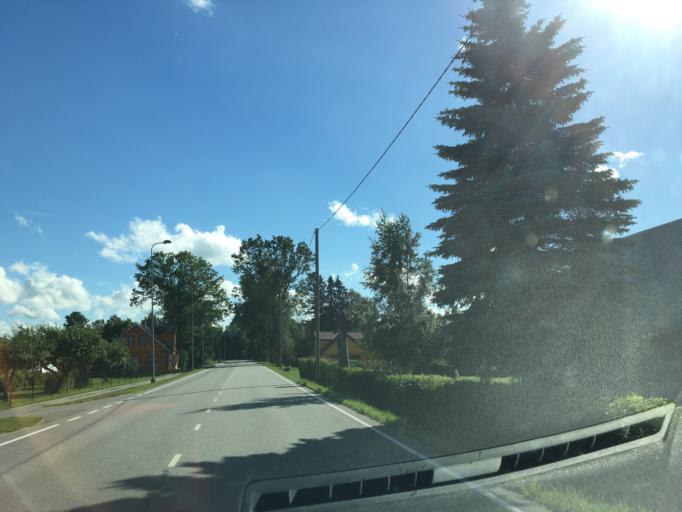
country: EE
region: Paernumaa
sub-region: Vaendra vald (alev)
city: Vandra
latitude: 58.6214
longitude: 25.1048
